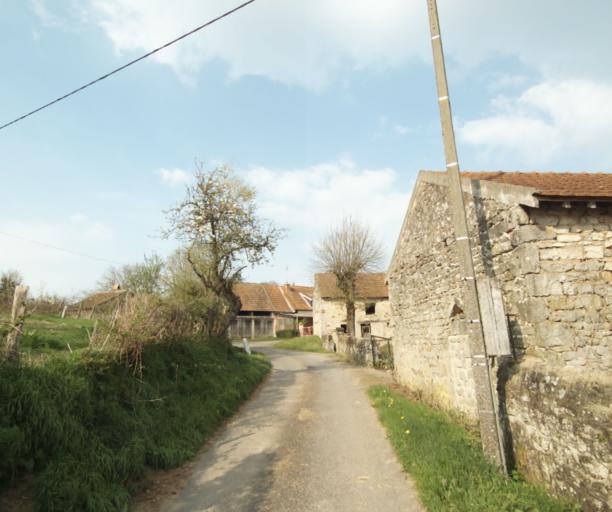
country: FR
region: Bourgogne
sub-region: Departement de Saone-et-Loire
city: Charolles
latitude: 46.4783
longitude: 4.4261
